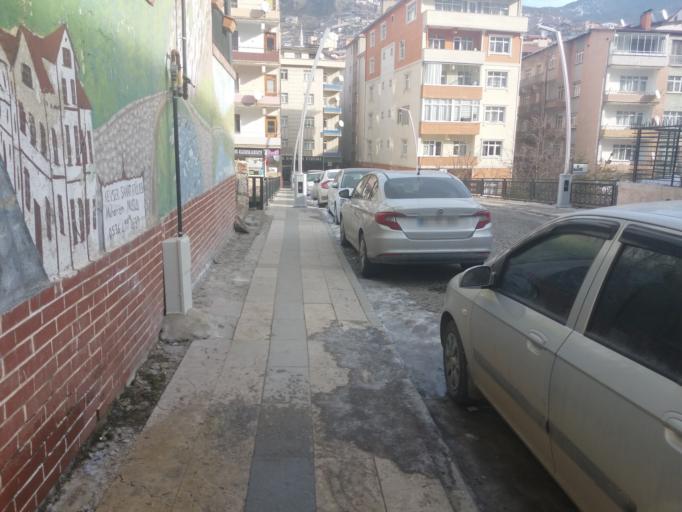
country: TR
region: Gumushane
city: Gumushkhane
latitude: 40.4605
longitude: 39.4732
